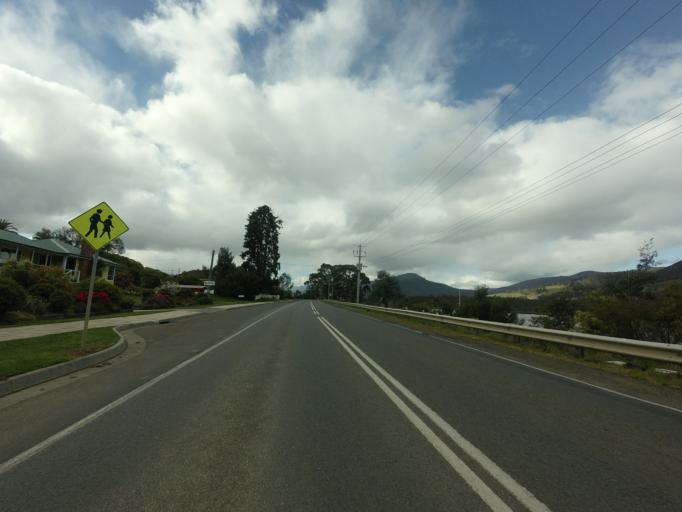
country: AU
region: Tasmania
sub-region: Huon Valley
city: Franklin
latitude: -43.0836
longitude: 147.0152
